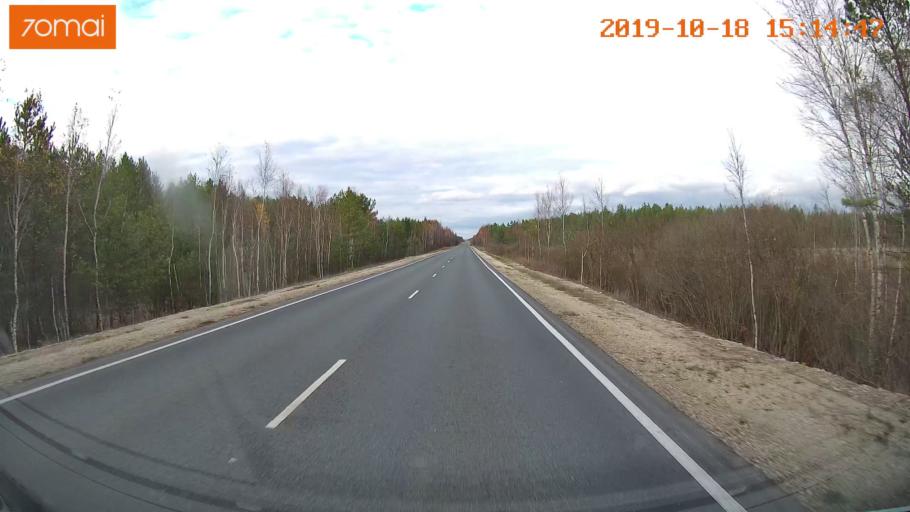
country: RU
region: Vladimir
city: Gus'-Khrustal'nyy
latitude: 55.6081
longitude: 40.7211
